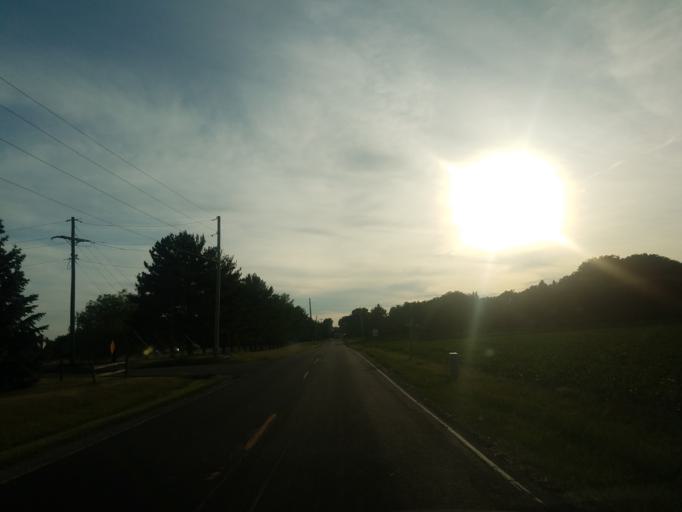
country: US
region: Illinois
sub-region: McLean County
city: Bloomington
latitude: 40.4440
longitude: -88.9759
